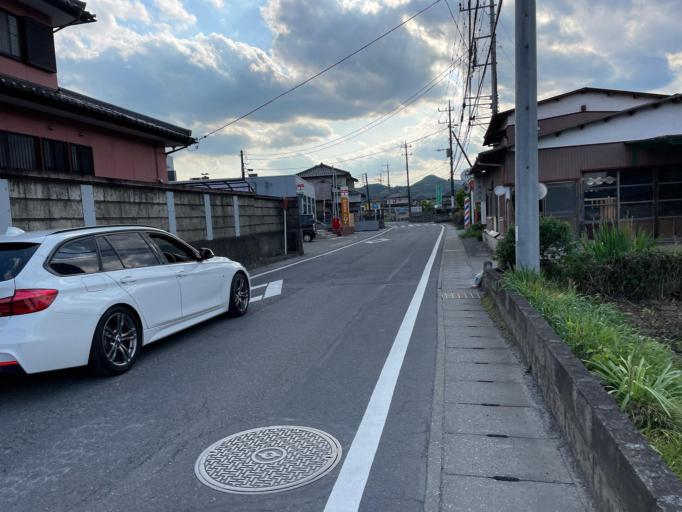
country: JP
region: Tochigi
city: Tochigi
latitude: 36.4114
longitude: 139.7073
